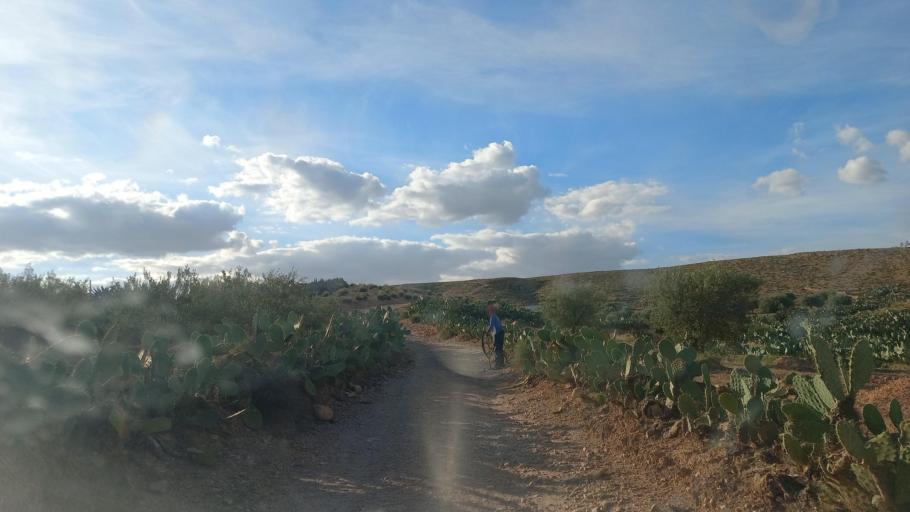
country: TN
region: Al Qasrayn
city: Sbiba
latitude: 35.3802
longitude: 9.0172
